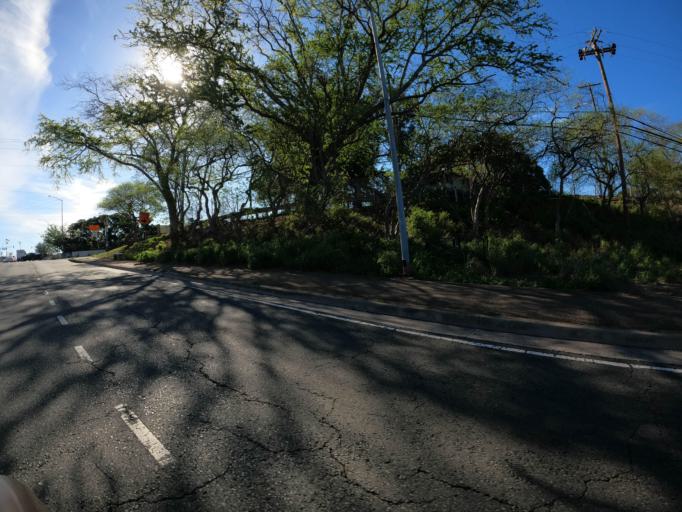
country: US
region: Hawaii
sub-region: Honolulu County
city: Halawa
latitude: 21.3525
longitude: -157.9335
